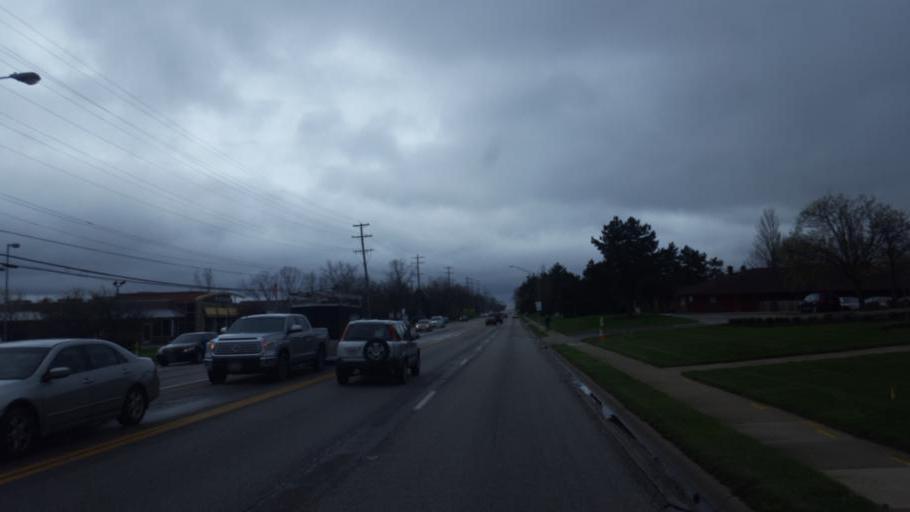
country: US
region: Ohio
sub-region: Franklin County
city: Westerville
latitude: 40.1245
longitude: -82.9483
